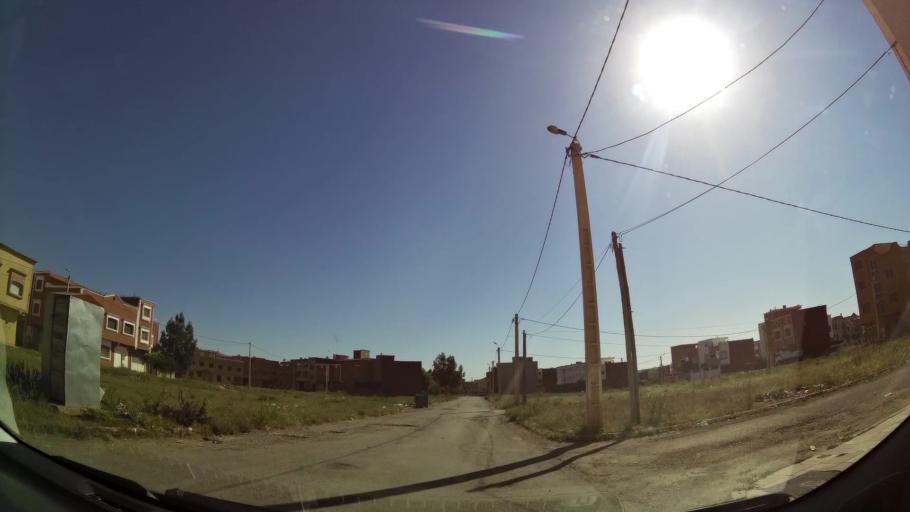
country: MA
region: Oriental
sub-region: Berkane-Taourirt
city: Berkane
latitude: 34.9409
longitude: -2.3370
